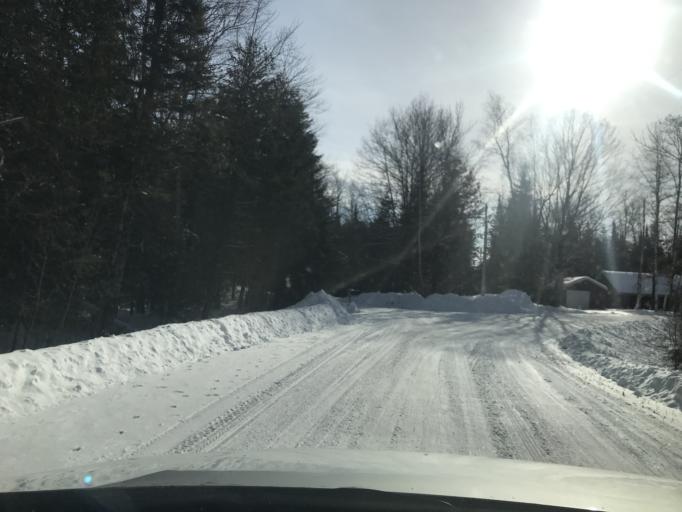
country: US
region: Wisconsin
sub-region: Oconto County
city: Gillett
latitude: 45.1468
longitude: -88.2280
